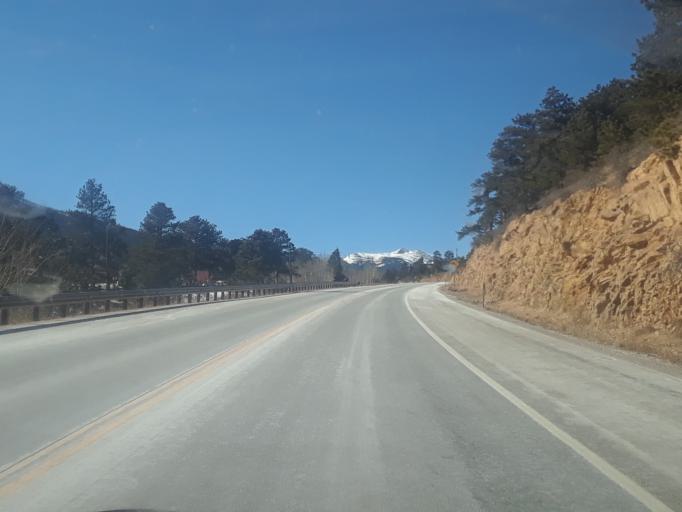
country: US
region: Colorado
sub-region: Larimer County
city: Estes Park
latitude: 40.1945
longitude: -105.5209
